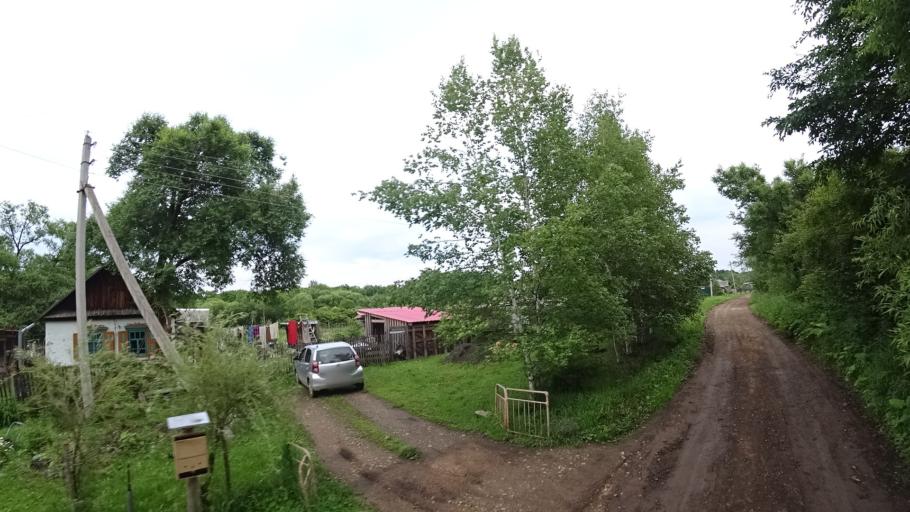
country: RU
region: Primorskiy
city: Novosysoyevka
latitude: 44.2386
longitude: 133.3786
